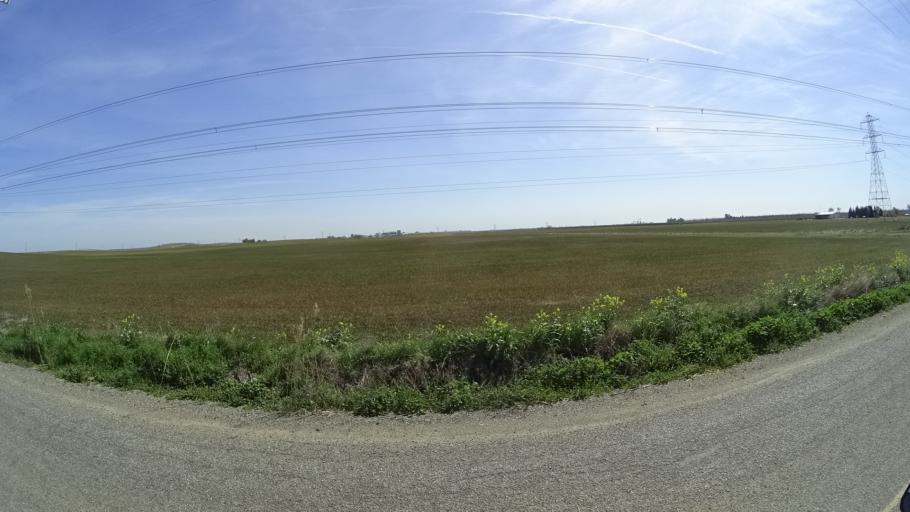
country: US
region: California
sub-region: Glenn County
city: Willows
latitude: 39.5350
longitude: -122.2872
